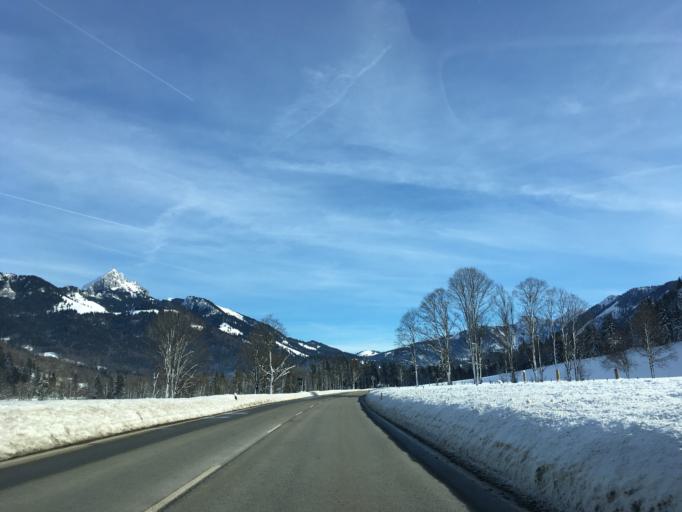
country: DE
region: Bavaria
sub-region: Upper Bavaria
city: Fischbachau
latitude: 47.7000
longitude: 11.9393
